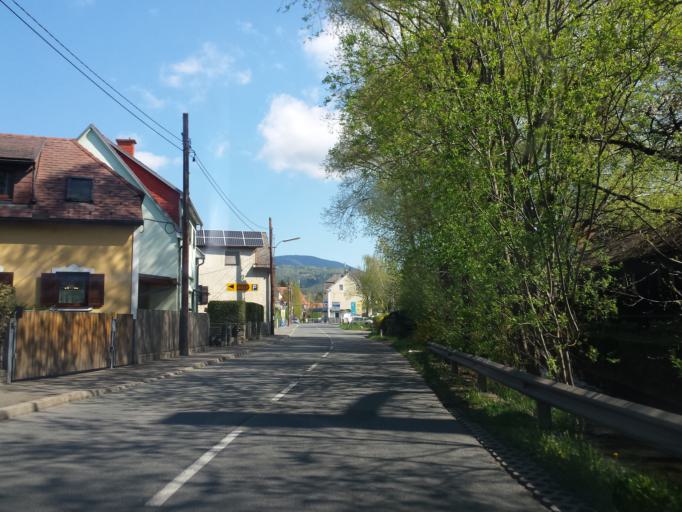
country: AT
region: Styria
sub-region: Politischer Bezirk Graz-Umgebung
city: Stattegg
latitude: 47.1122
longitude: 15.4229
